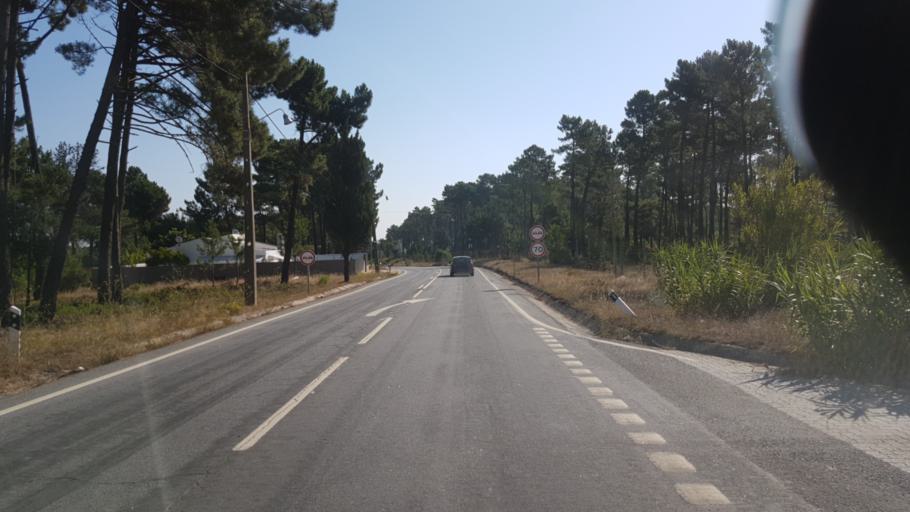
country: PT
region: Setubal
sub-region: Sesimbra
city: Sesimbra
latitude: 38.4875
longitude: -9.0625
